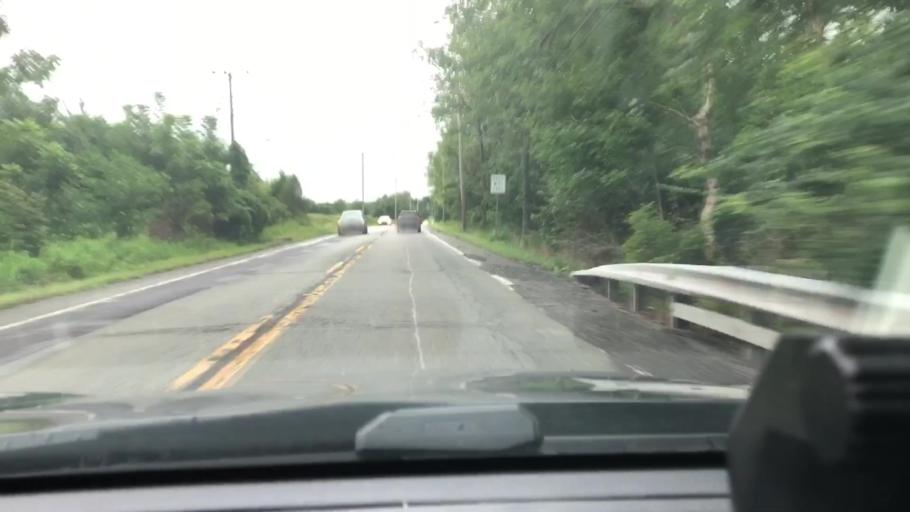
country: US
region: Pennsylvania
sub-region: Montgomery County
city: Gilbertsville
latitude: 40.3235
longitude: -75.5623
